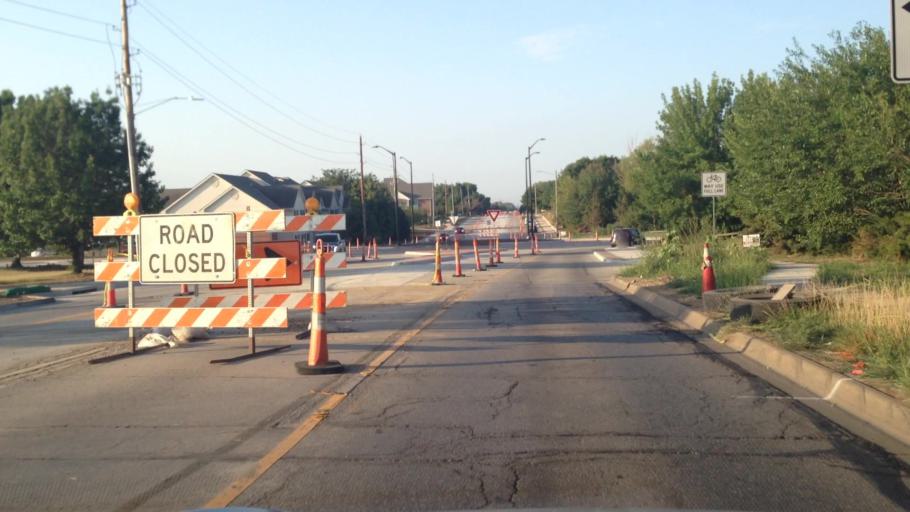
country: US
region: Kansas
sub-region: Douglas County
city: Lawrence
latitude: 38.9686
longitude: -95.3070
